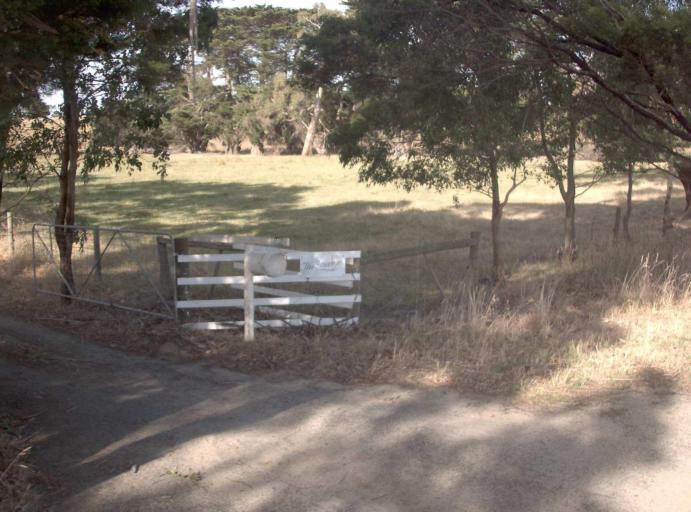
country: AU
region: Victoria
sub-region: Latrobe
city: Morwell
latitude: -38.2936
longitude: 146.4498
